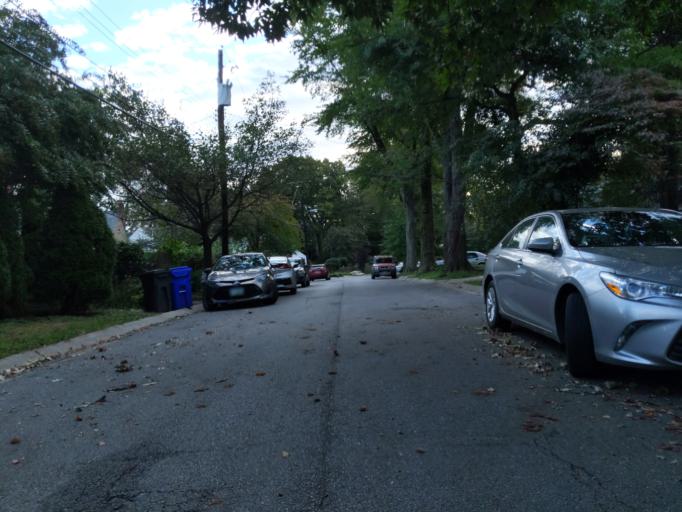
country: US
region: Maryland
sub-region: Montgomery County
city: Forest Glen
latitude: 39.0122
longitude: -77.0447
